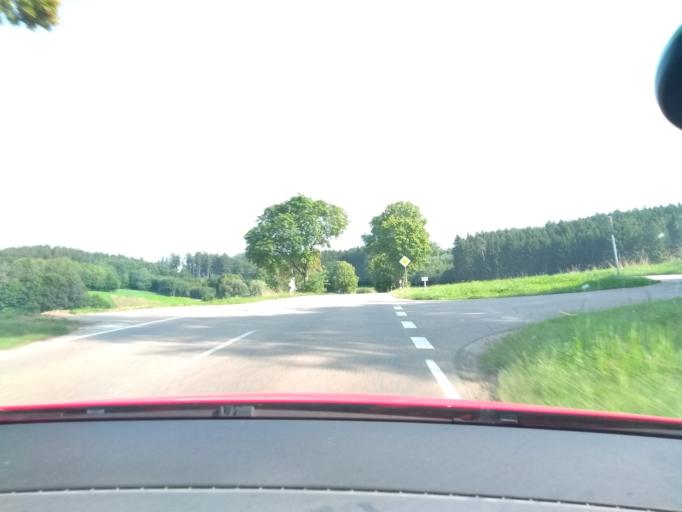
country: DE
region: Bavaria
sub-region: Upper Bavaria
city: Altomunster
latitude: 48.4034
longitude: 11.2983
